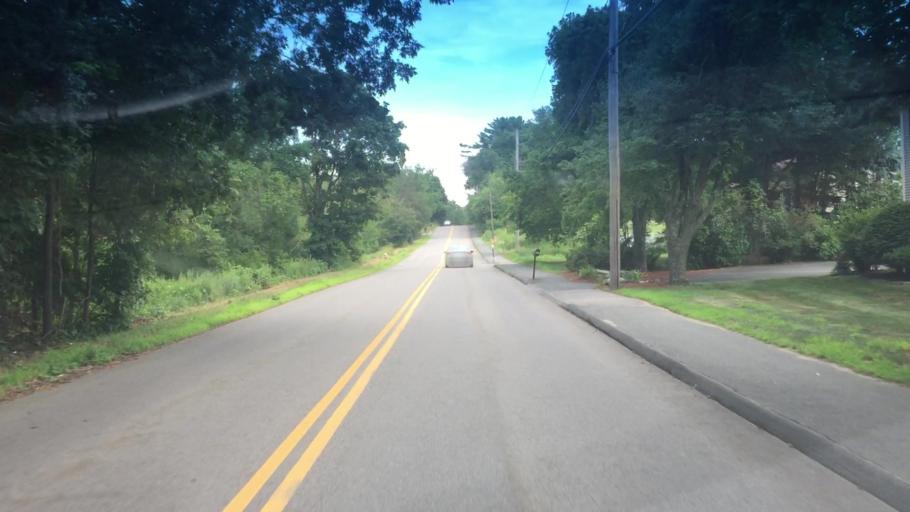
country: US
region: Massachusetts
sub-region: Norfolk County
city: Medway
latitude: 42.1205
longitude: -71.3971
